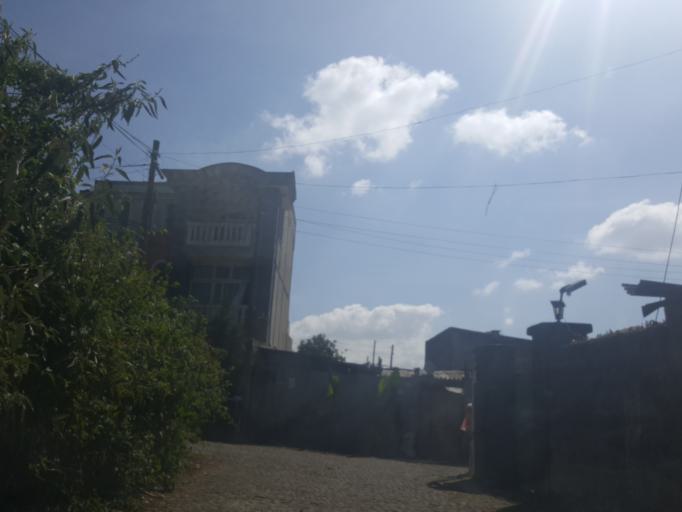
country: ET
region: Adis Abeba
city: Addis Ababa
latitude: 9.0663
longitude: 38.7237
